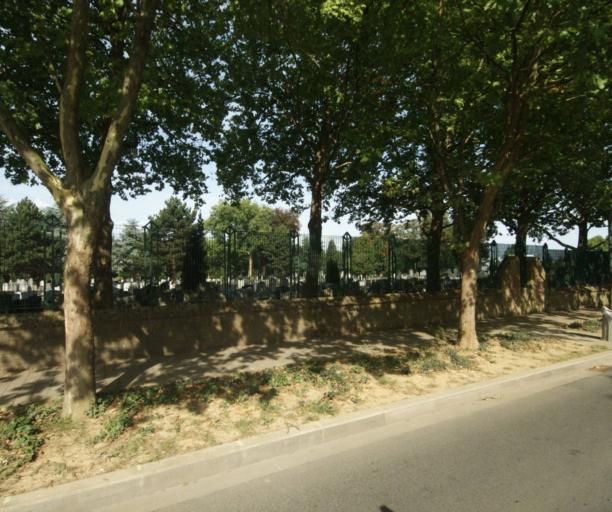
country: FR
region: Nord-Pas-de-Calais
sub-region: Departement du Nord
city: Lille
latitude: 50.6095
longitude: 3.0543
